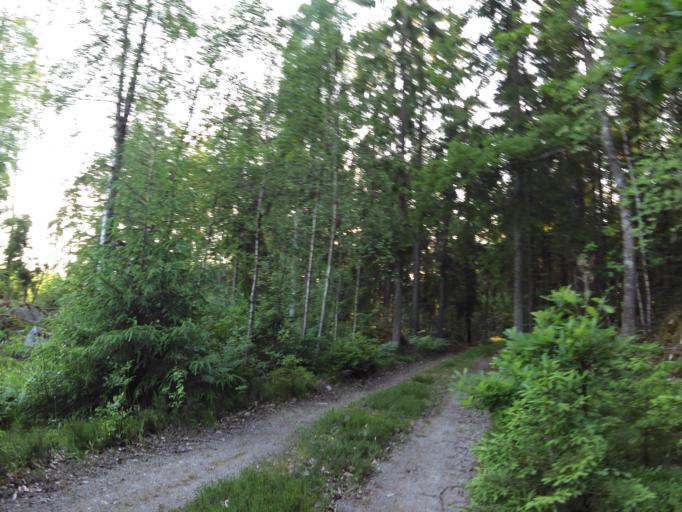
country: SE
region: Blekinge
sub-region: Olofstroms Kommun
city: Olofstroem
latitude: 56.4130
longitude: 14.5570
